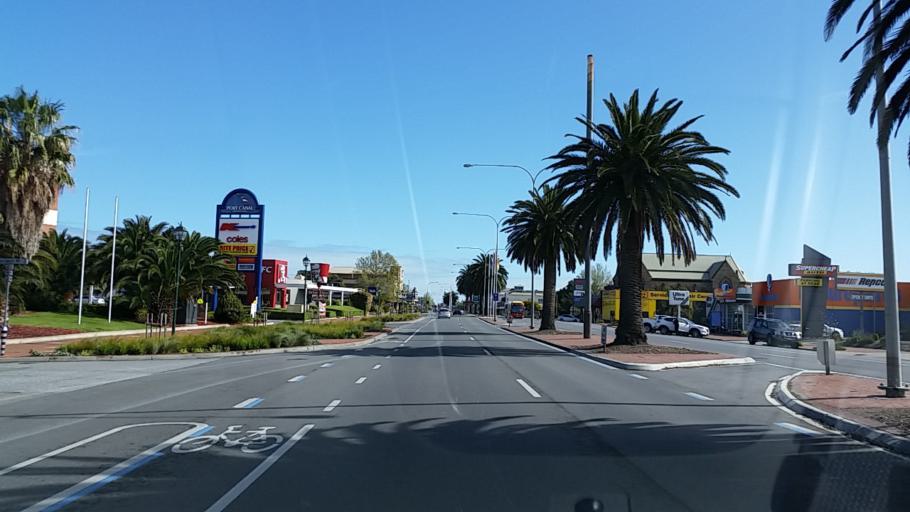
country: AU
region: South Australia
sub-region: Port Adelaide Enfield
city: Birkenhead
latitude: -34.8485
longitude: 138.5080
